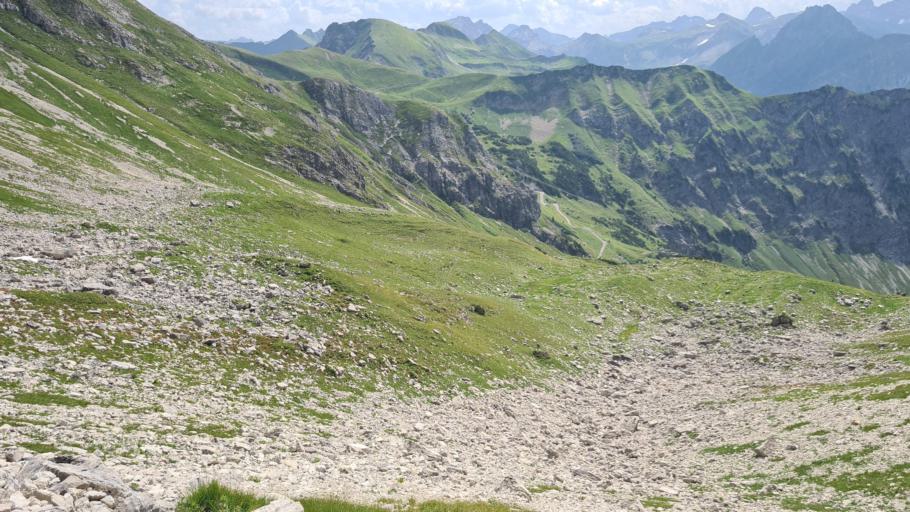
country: DE
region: Bavaria
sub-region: Swabia
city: Oberstdorf
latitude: 47.4196
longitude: 10.3353
